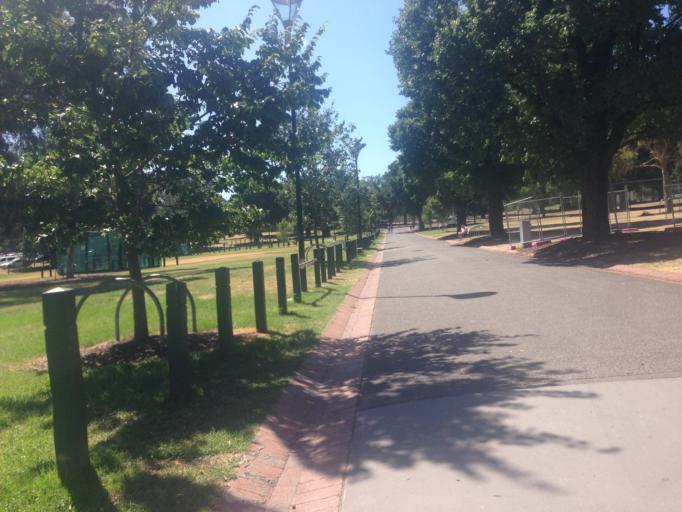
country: AU
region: Victoria
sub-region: Melbourne
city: East Melbourne
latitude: -37.8184
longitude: 144.9841
